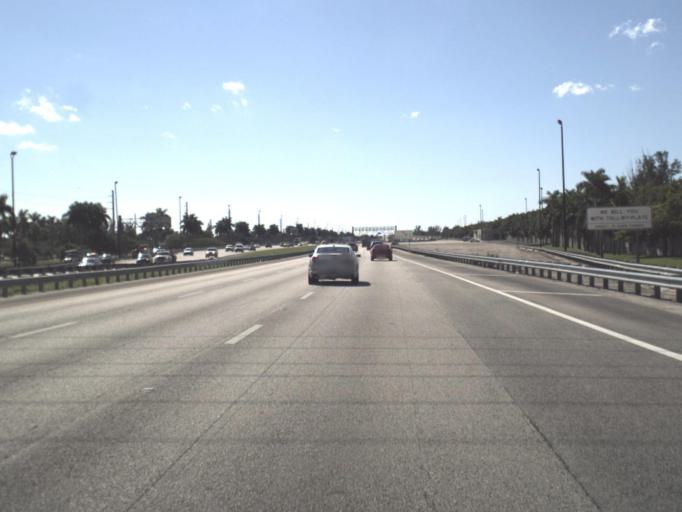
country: US
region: Florida
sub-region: Miami-Dade County
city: Westwood Lake
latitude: 25.7289
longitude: -80.3843
